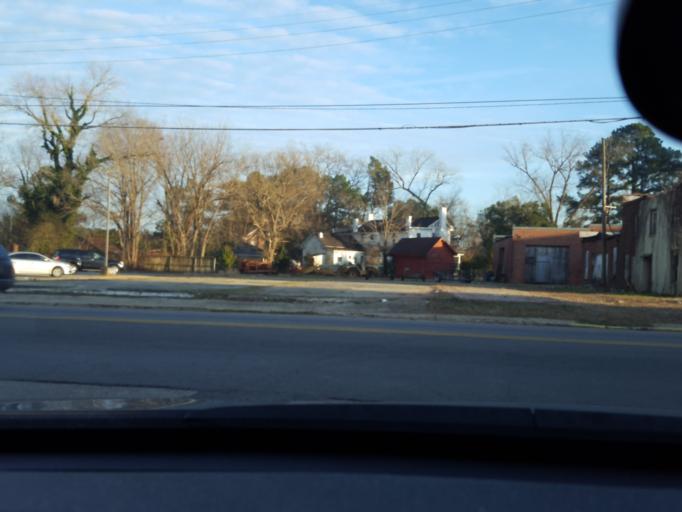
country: US
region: North Carolina
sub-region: Northampton County
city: Jackson
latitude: 36.2741
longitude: -77.2843
